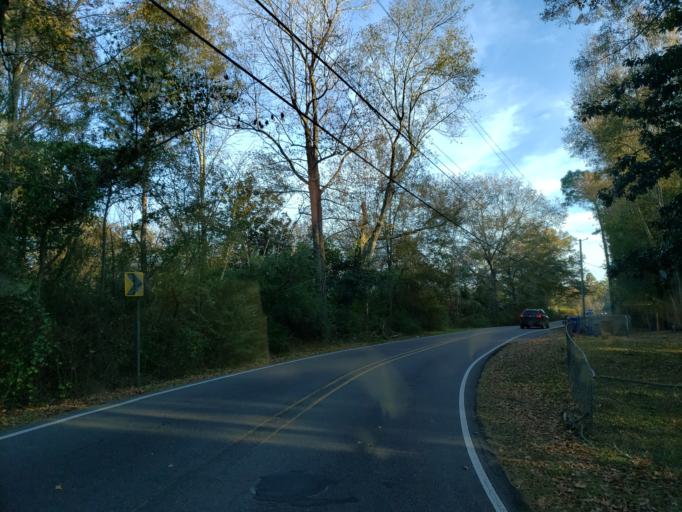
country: US
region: Mississippi
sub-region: Lamar County
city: Arnold Line
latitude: 31.3434
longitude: -89.3457
